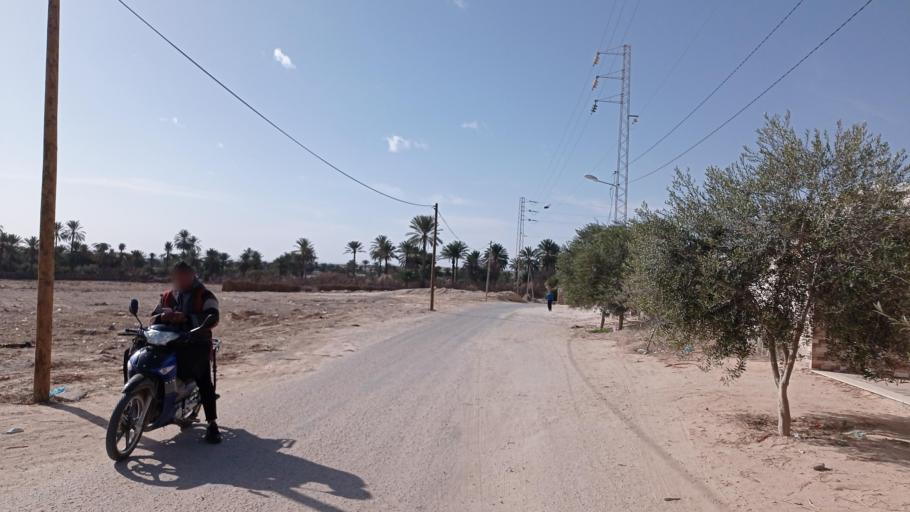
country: TN
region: Qabis
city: Gabes
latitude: 33.8366
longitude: 10.1145
